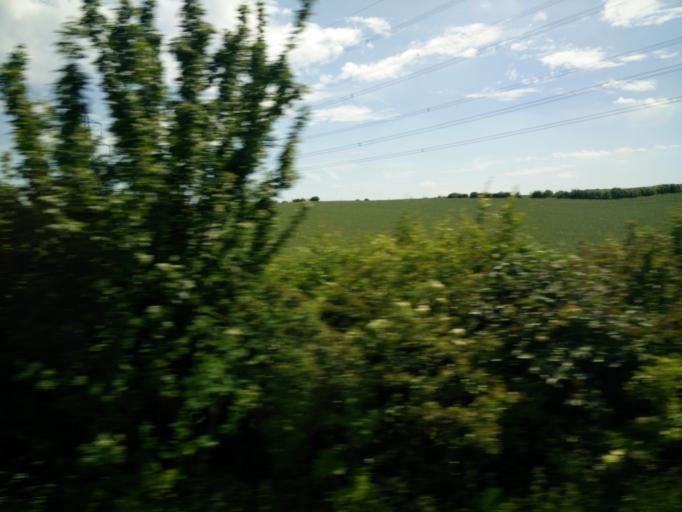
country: GB
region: England
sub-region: Hertfordshire
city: Hitchin
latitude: 51.9365
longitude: -0.3202
